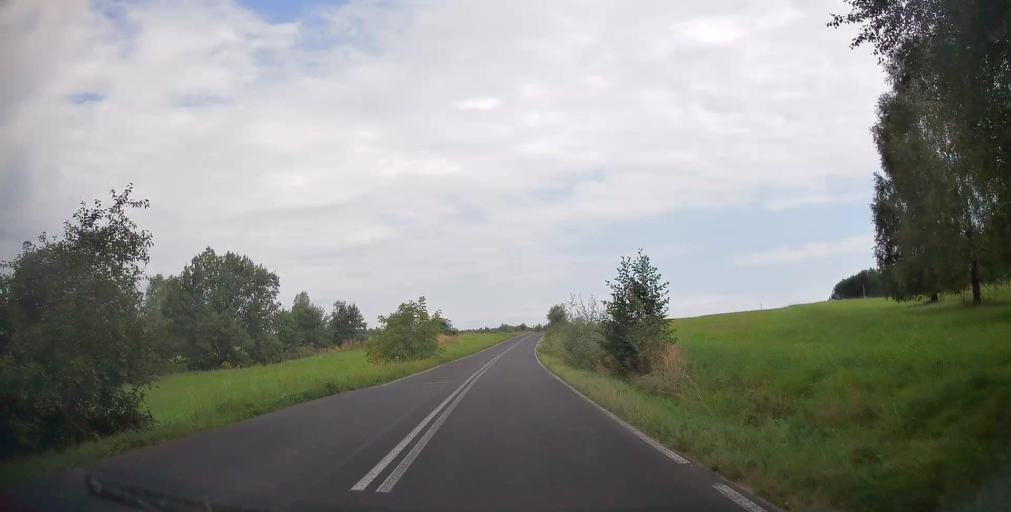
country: PL
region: Lesser Poland Voivodeship
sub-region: Powiat chrzanowski
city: Grojec
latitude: 50.0820
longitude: 19.5551
